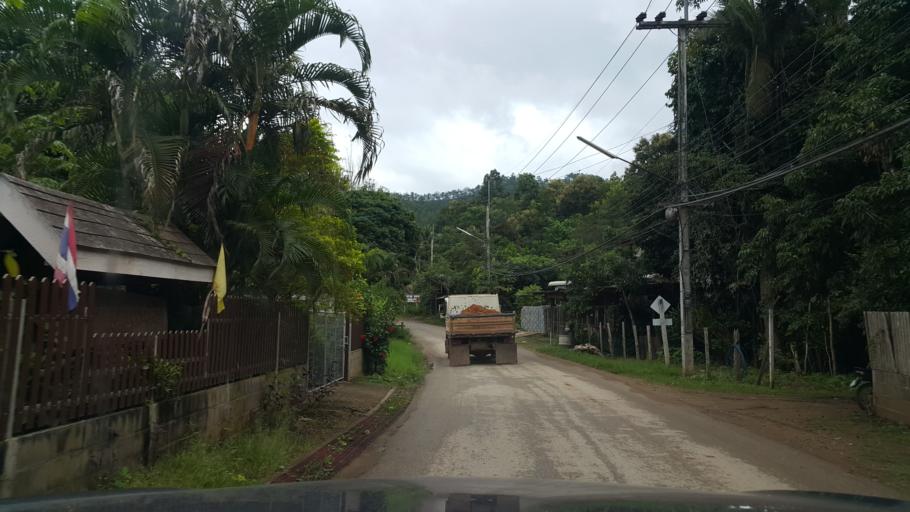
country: TH
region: Chiang Mai
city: Samoeng
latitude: 18.8588
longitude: 98.7313
